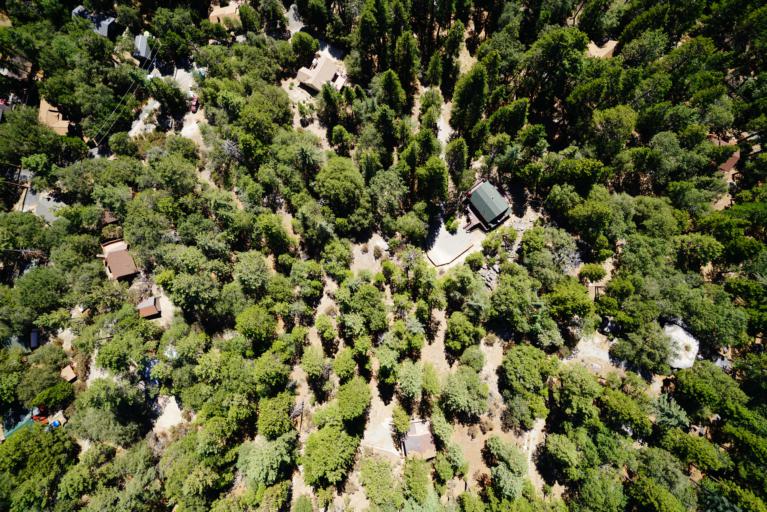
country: US
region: California
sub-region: Riverside County
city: Idyllwild-Pine Cove
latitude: 33.7585
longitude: -116.7455
